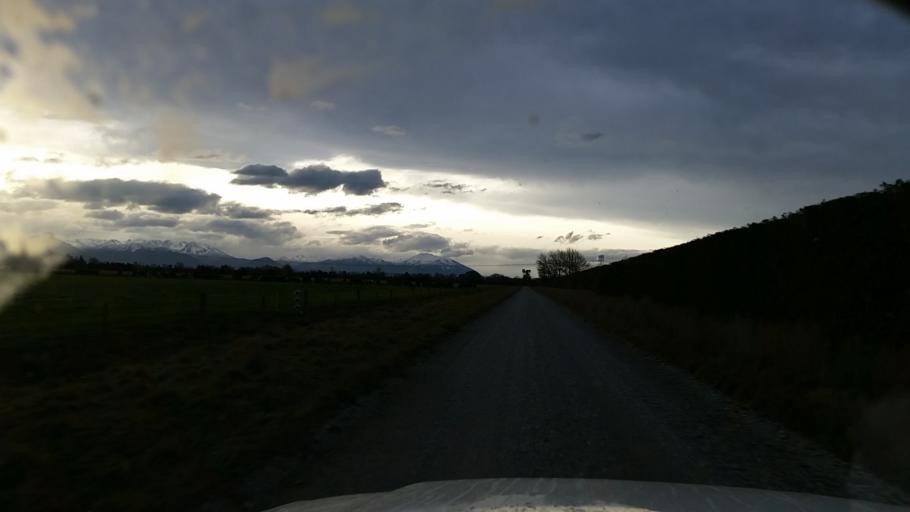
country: NZ
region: Canterbury
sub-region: Ashburton District
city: Ashburton
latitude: -43.8554
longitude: 171.6622
